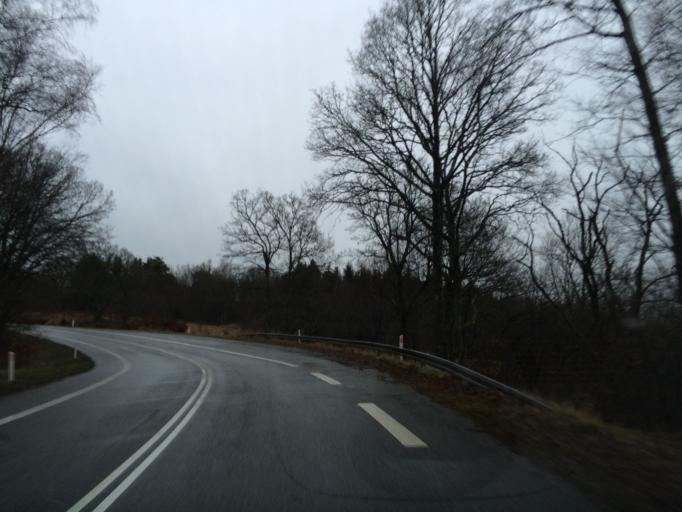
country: DK
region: North Denmark
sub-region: Rebild Kommune
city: Stovring
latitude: 56.8281
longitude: 9.8172
